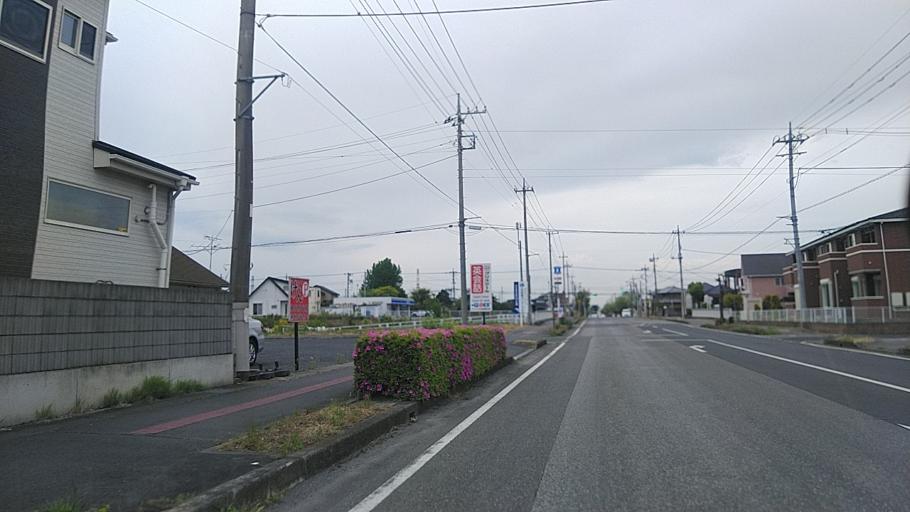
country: JP
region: Gunma
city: Ota
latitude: 36.2754
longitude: 139.3560
